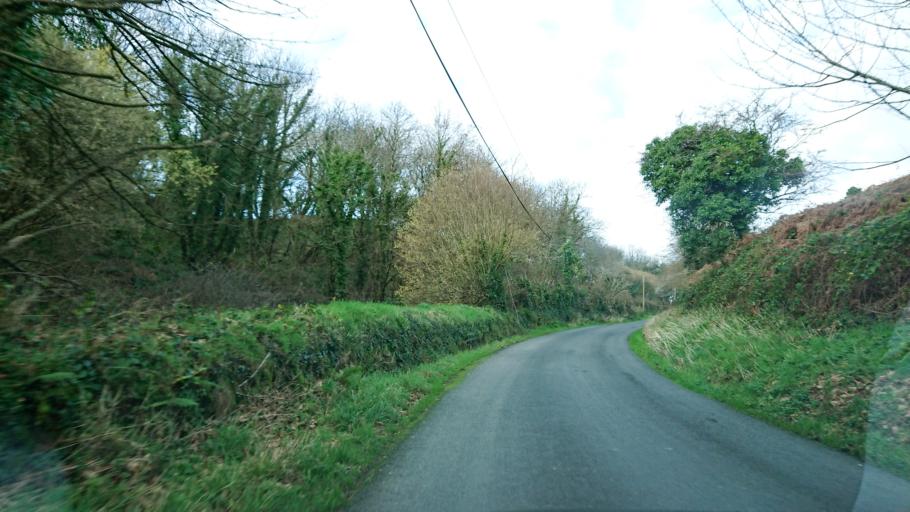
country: IE
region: Munster
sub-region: Waterford
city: Tra Mhor
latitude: 52.1571
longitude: -7.2672
